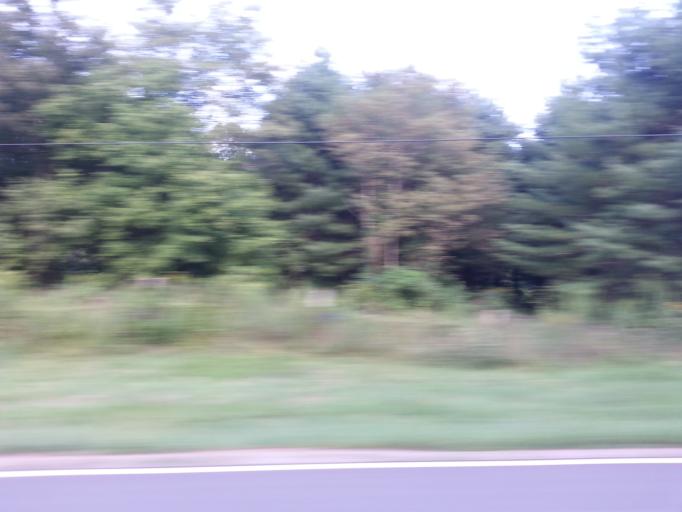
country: US
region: Tennessee
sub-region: Johnson County
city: Mountain City
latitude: 36.6052
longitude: -81.8106
